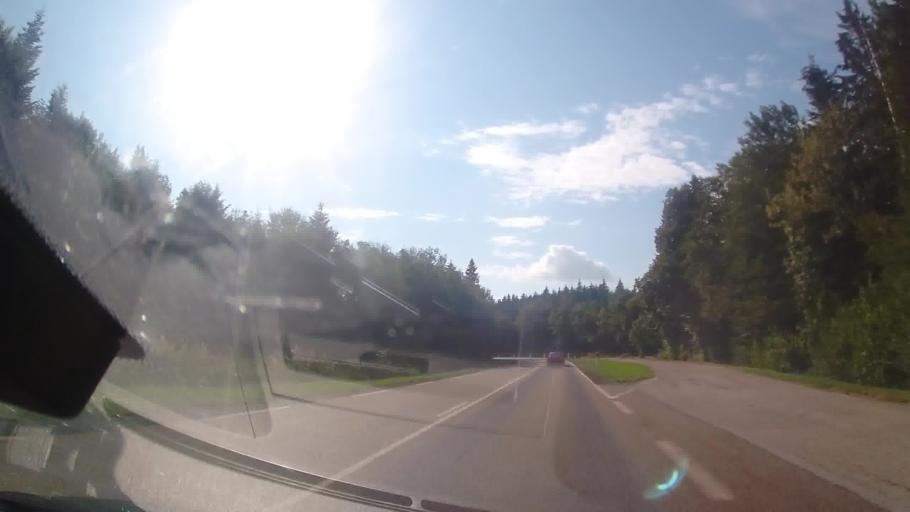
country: FR
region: Franche-Comte
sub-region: Departement du Jura
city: Clairvaux-les-Lacs
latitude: 46.5838
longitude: 5.8096
